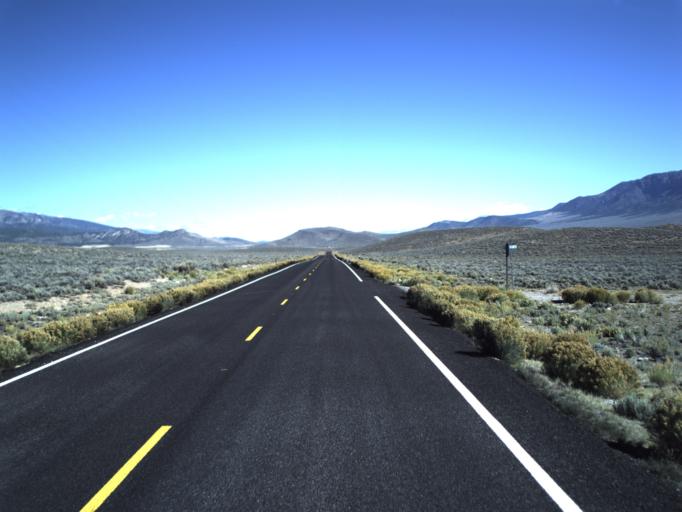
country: US
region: Utah
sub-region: Piute County
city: Junction
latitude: 38.2193
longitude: -112.0002
